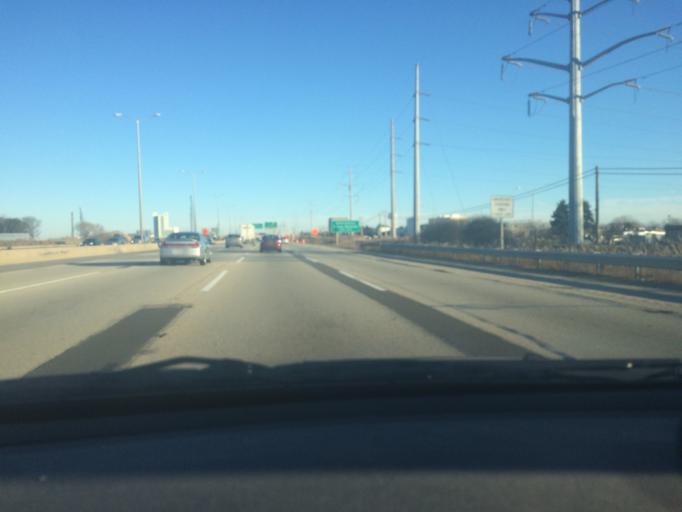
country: US
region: Illinois
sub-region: Cook County
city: Hoffman Estates
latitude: 42.0609
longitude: -88.0567
